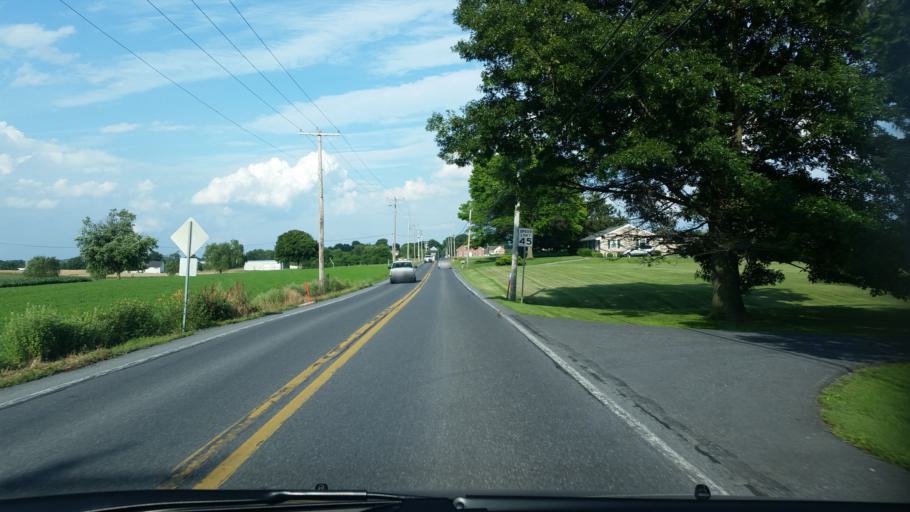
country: US
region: Pennsylvania
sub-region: Lancaster County
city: Lititz
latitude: 40.1535
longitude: -76.3361
